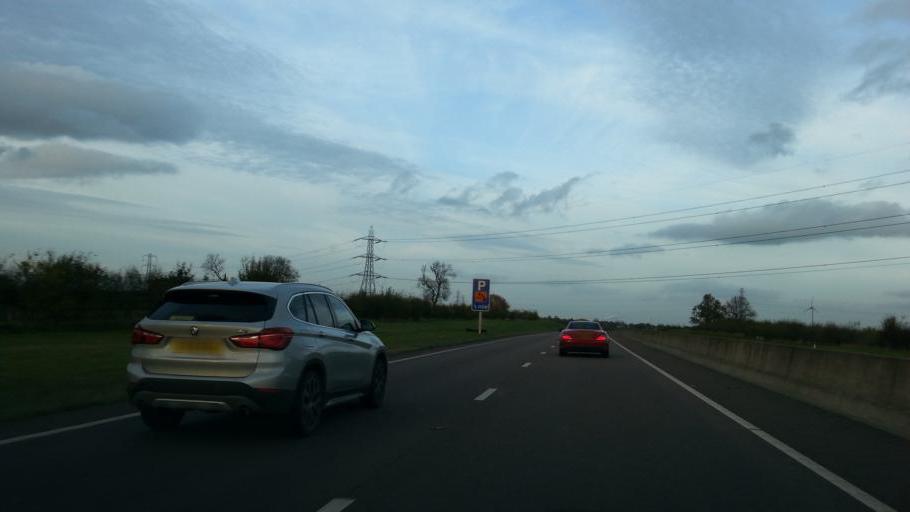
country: GB
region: England
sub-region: Nottinghamshire
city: Farndon
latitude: 53.0405
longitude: -0.8669
